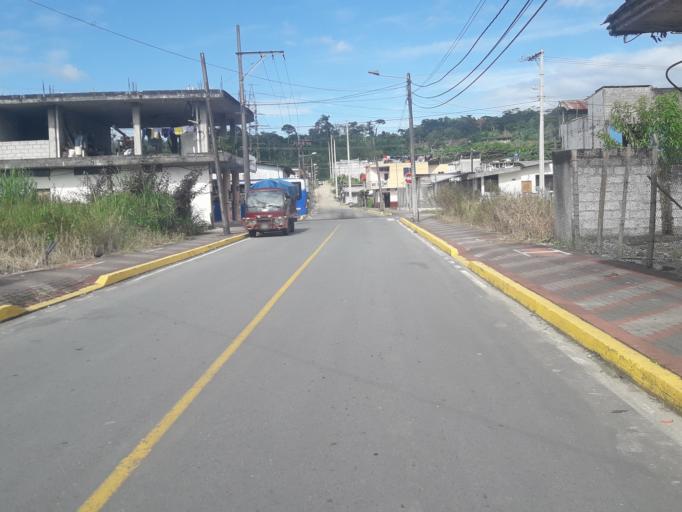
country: EC
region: Napo
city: Tena
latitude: -1.0080
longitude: -77.8133
